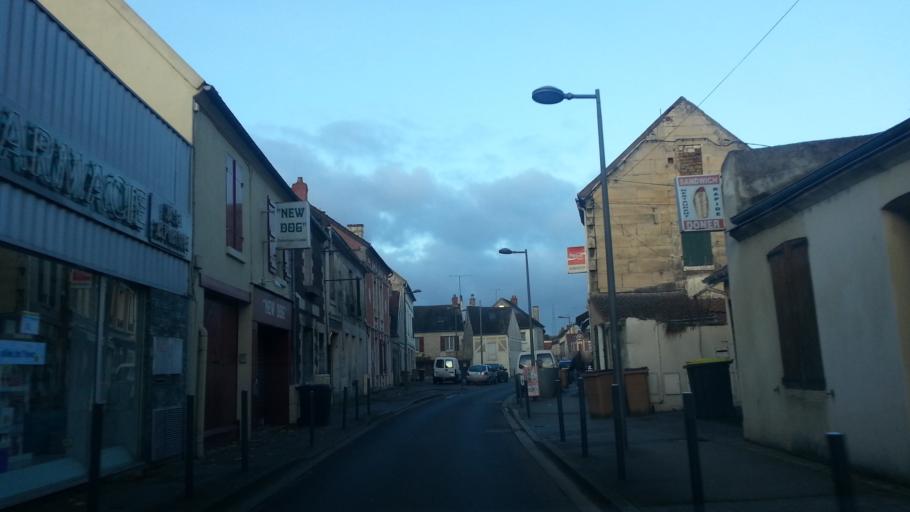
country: FR
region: Picardie
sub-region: Departement de l'Oise
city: Montataire
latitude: 49.2568
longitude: 2.4331
